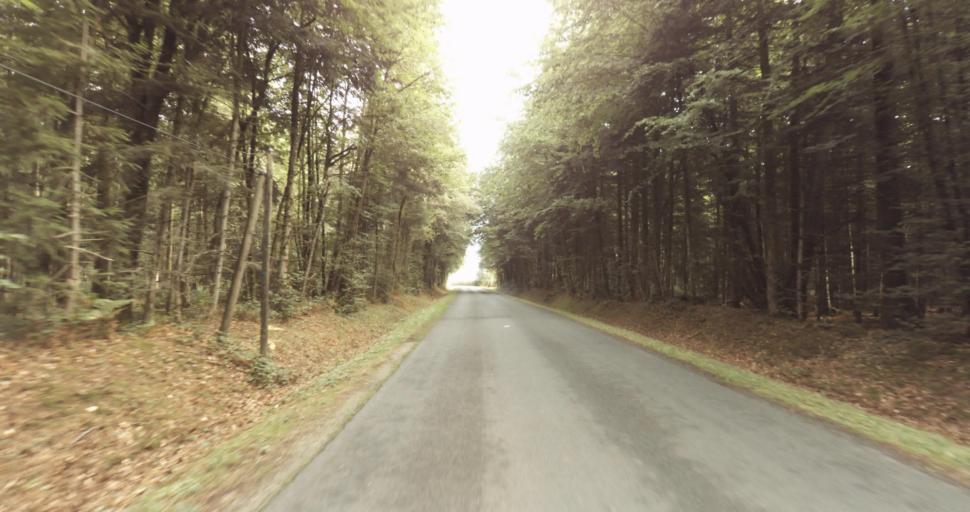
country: FR
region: Lower Normandy
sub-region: Departement de l'Orne
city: Gace
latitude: 48.8235
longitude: 0.2364
